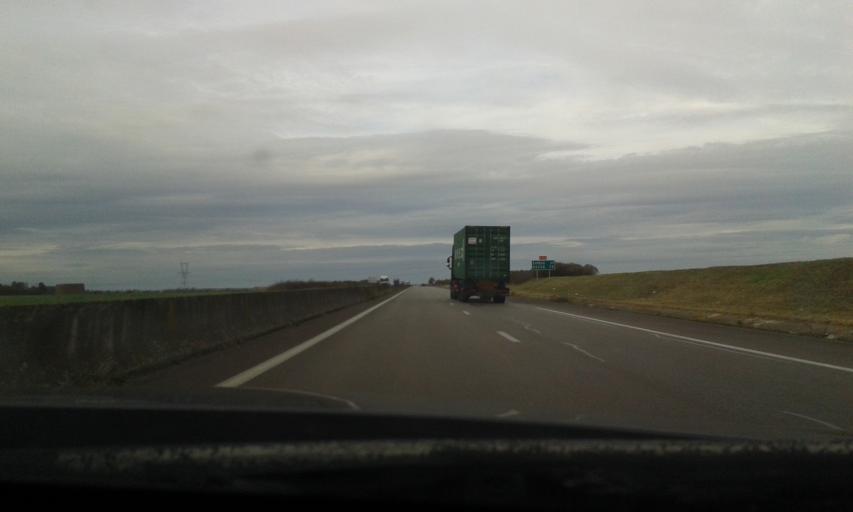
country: FR
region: Haute-Normandie
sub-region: Departement de l'Eure
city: La Madeleine-de-Nonancourt
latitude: 48.8430
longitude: 1.1818
